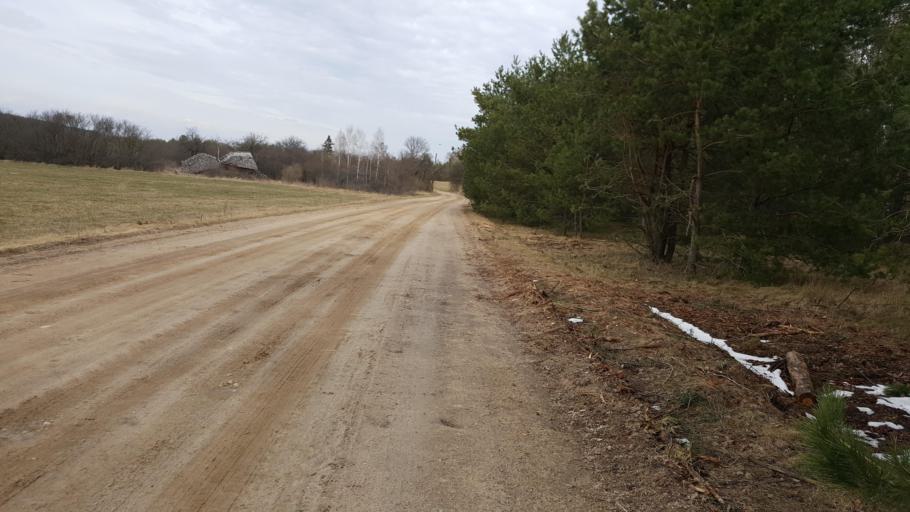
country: BY
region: Brest
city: Kamyanyets
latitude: 52.3709
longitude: 23.9790
